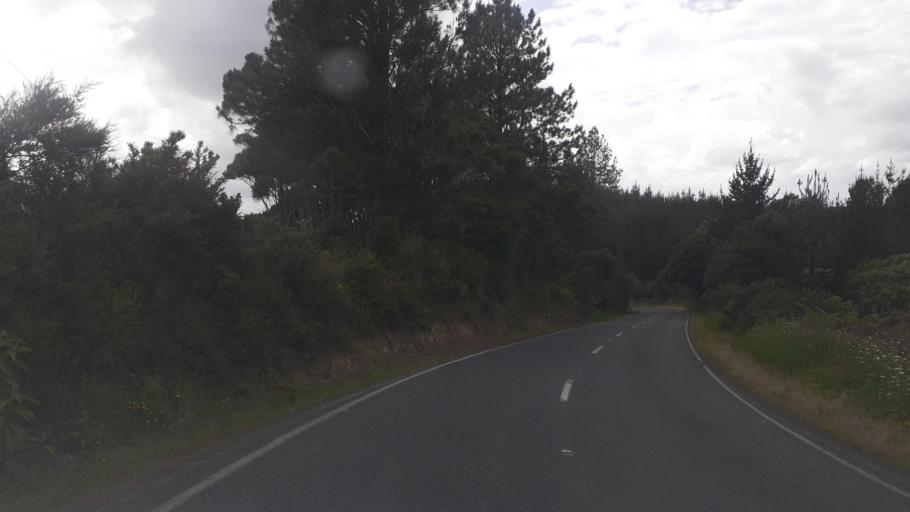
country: NZ
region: Northland
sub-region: Far North District
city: Kerikeri
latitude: -35.2249
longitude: 174.0047
